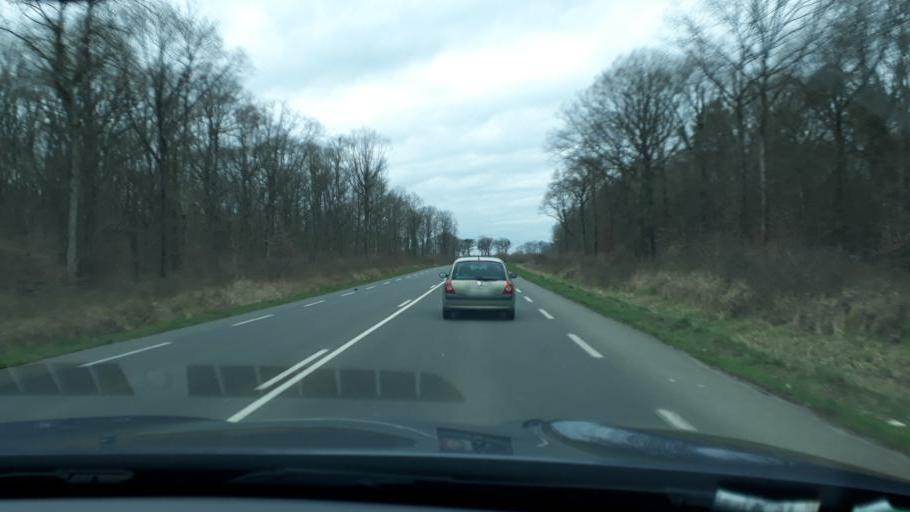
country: FR
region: Centre
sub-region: Departement du Loiret
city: Chanteau
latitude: 47.9994
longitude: 1.9465
